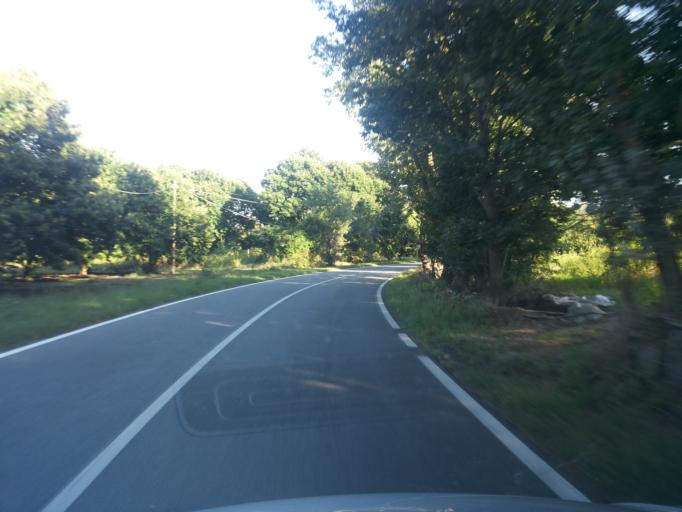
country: IT
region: Piedmont
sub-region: Provincia di Vercelli
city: Borgo d'Ale
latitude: 45.3628
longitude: 8.0391
